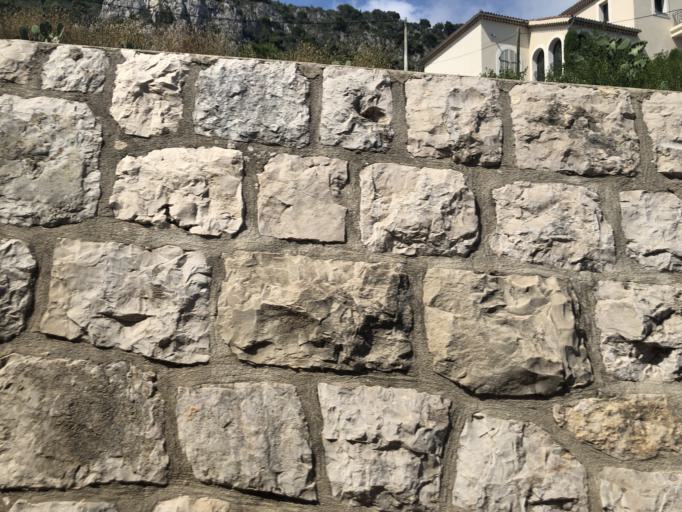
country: FR
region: Provence-Alpes-Cote d'Azur
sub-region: Departement des Alpes-Maritimes
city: Beaulieu-sur-Mer
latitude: 43.7103
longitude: 7.3274
